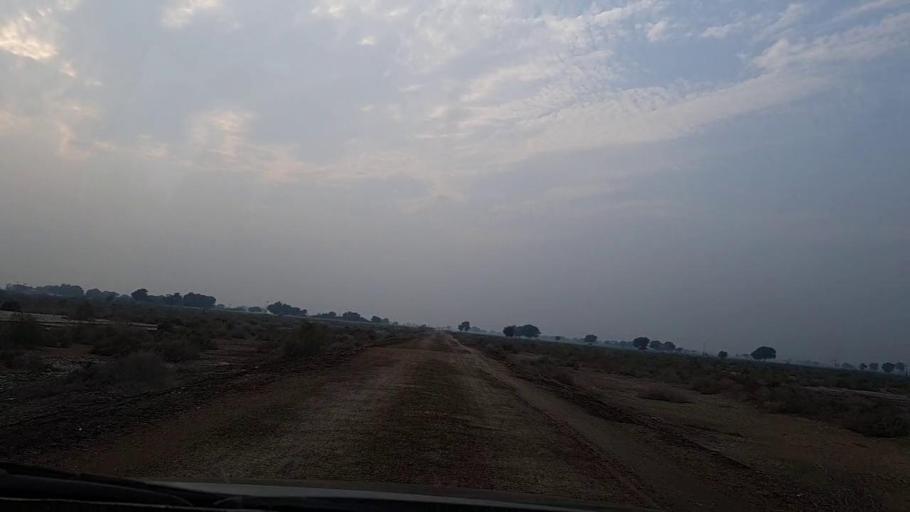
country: PK
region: Sindh
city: Nawabshah
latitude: 26.2736
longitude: 68.3481
